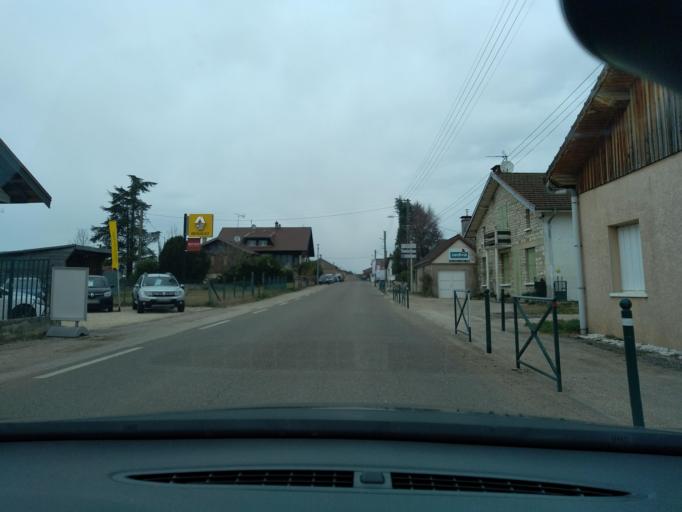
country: FR
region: Franche-Comte
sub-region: Departement du Jura
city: Arinthod
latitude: 46.3887
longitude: 5.5644
